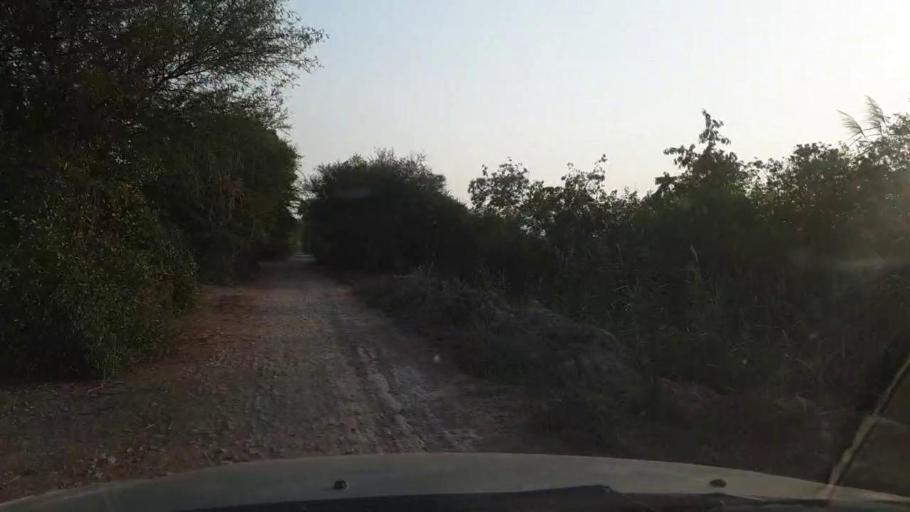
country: PK
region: Sindh
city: Tando Muhammad Khan
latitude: 25.0083
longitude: 68.4359
